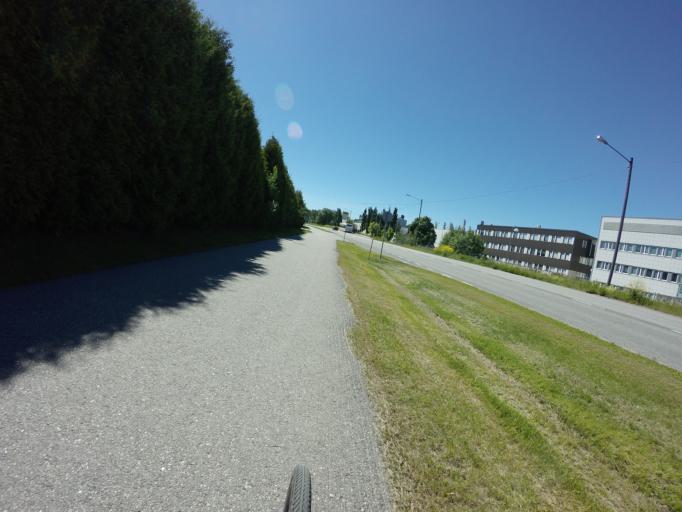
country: FI
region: Varsinais-Suomi
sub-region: Turku
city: Turku
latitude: 60.4802
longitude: 22.2988
